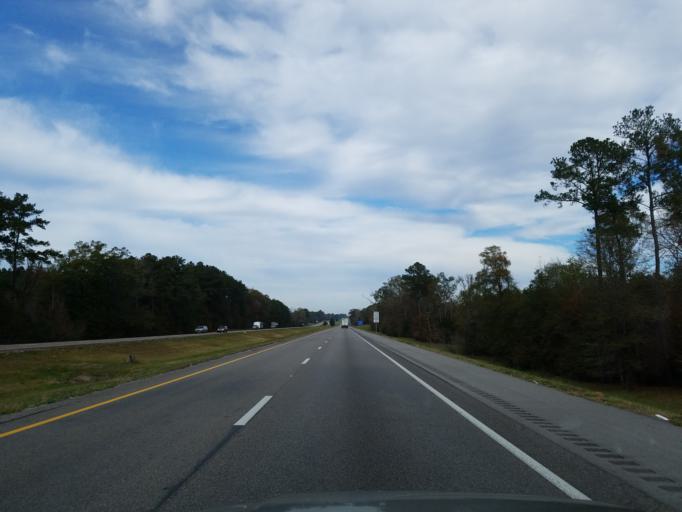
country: US
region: Mississippi
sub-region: Jones County
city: Sharon
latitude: 31.7916
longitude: -89.0545
